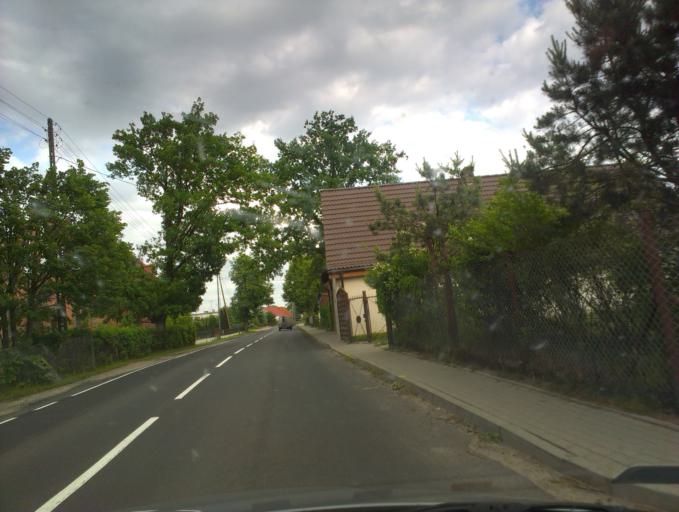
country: PL
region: West Pomeranian Voivodeship
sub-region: Powiat szczecinecki
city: Szczecinek
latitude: 53.6519
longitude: 16.6269
